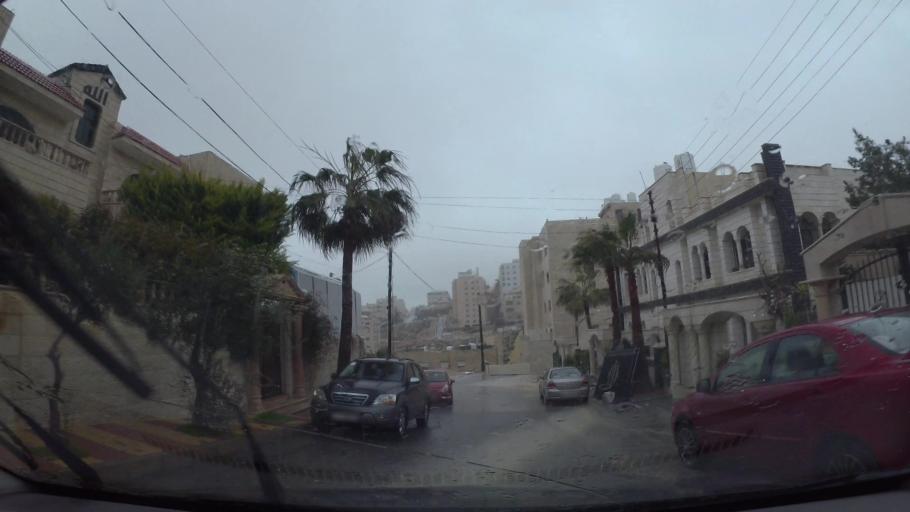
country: JO
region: Amman
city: Al Jubayhah
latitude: 32.0104
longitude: 35.8871
